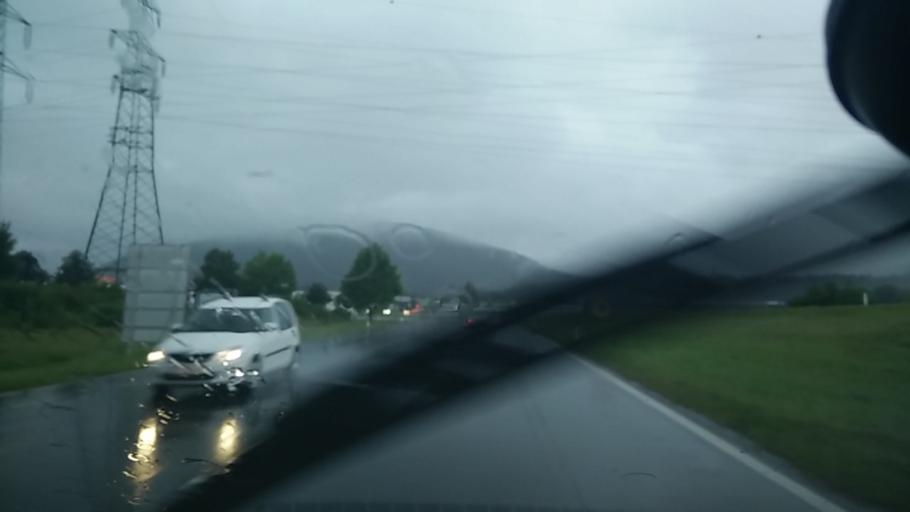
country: AT
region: Carinthia
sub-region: Villach Stadt
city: Villach
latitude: 46.5934
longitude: 13.8359
